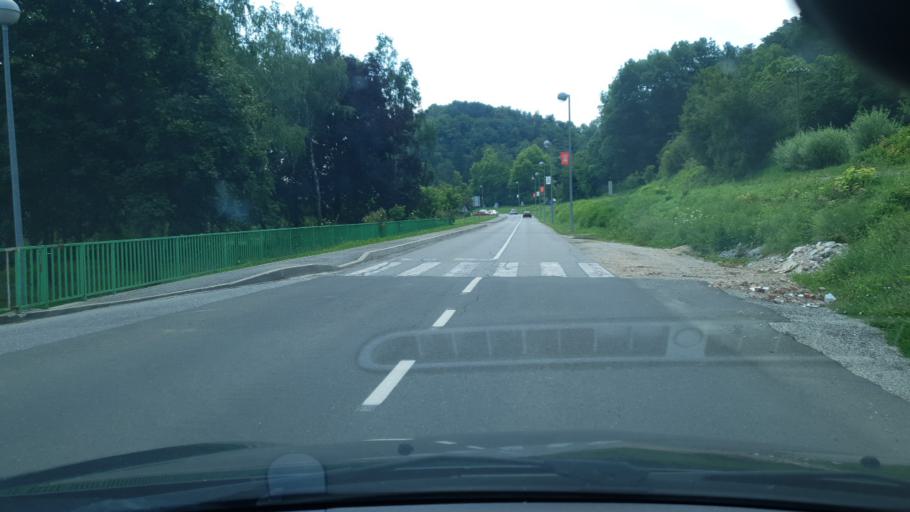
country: HR
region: Krapinsko-Zagorska
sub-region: Grad Krapina
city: Krapina
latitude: 46.1682
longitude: 15.8623
